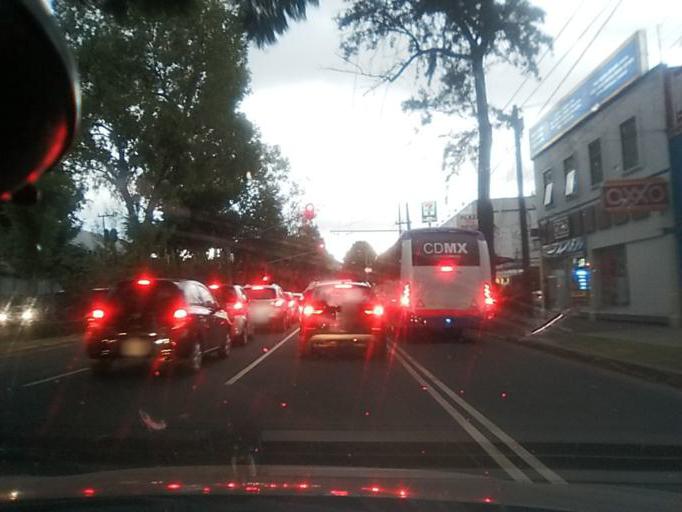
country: MX
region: Mexico City
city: Coyoacan
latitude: 19.3451
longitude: -99.1672
